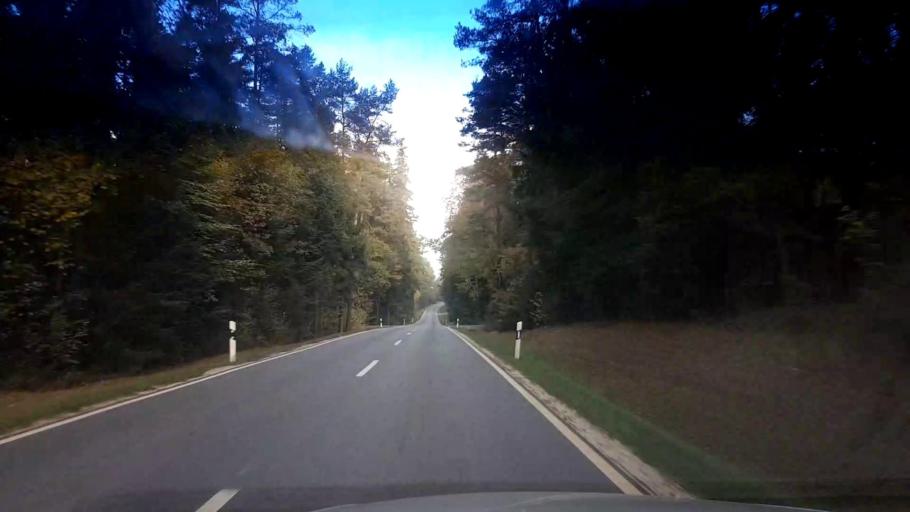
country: DE
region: Bavaria
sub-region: Upper Franconia
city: Weismain
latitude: 50.0988
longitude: 11.2545
